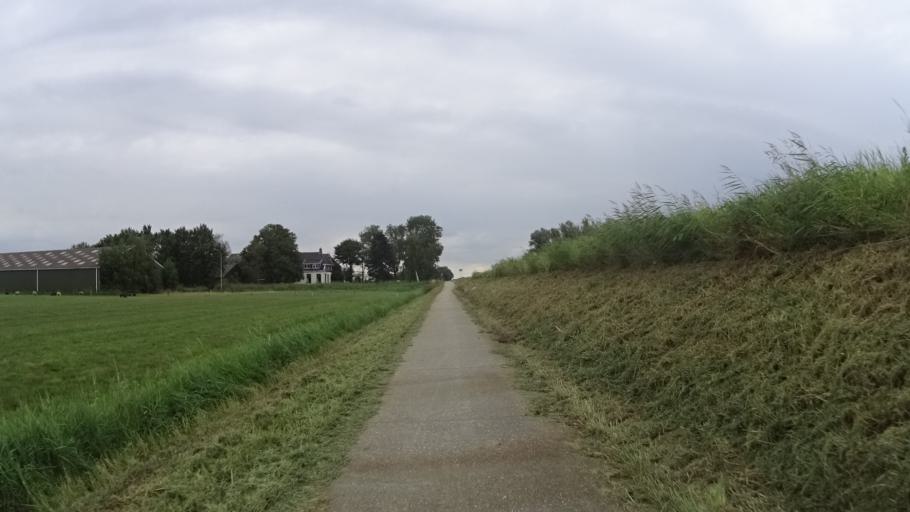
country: NL
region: Groningen
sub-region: Gemeente Haren
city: Haren
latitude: 53.2356
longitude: 6.6813
